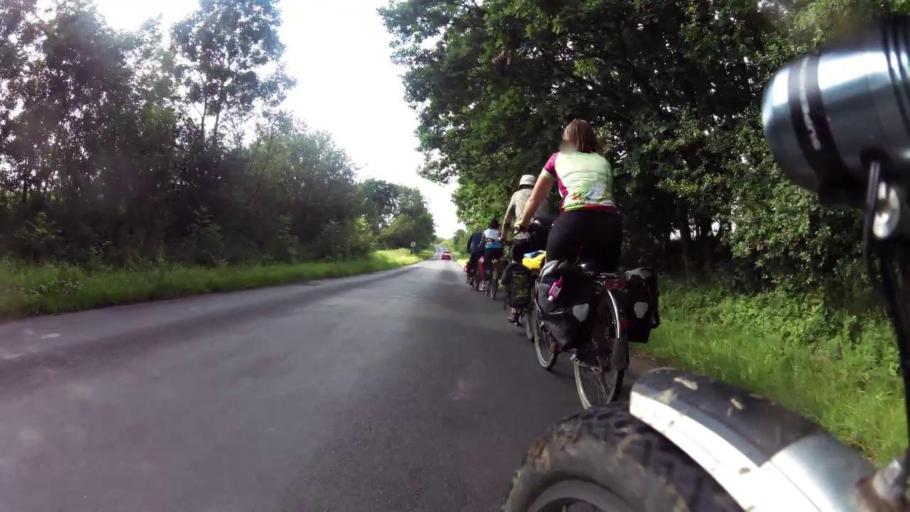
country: PL
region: West Pomeranian Voivodeship
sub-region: Powiat gryfinski
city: Gryfino
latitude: 53.2345
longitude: 14.5177
